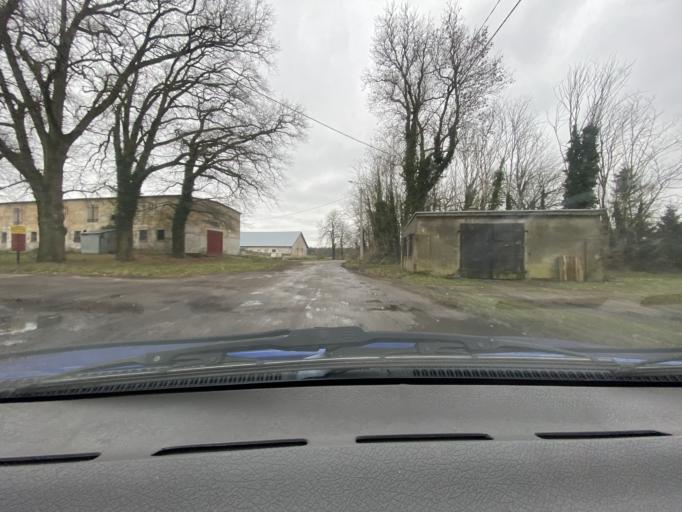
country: PL
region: West Pomeranian Voivodeship
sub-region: Powiat gryficki
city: Gryfice
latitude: 53.9494
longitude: 15.2658
